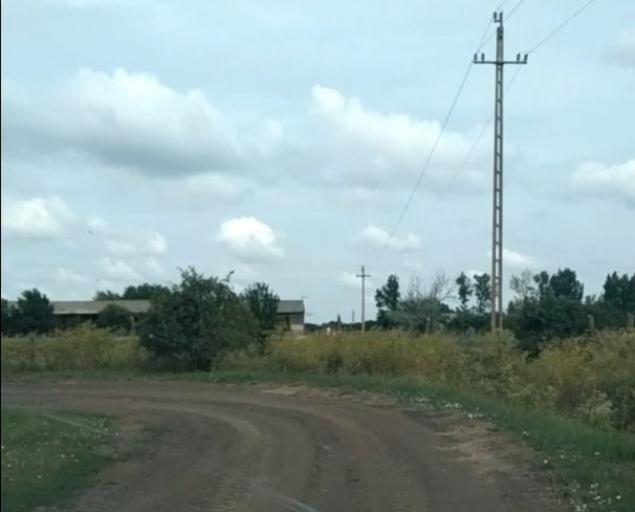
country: HU
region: Bekes
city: Szarvas
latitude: 46.8063
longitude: 20.5234
